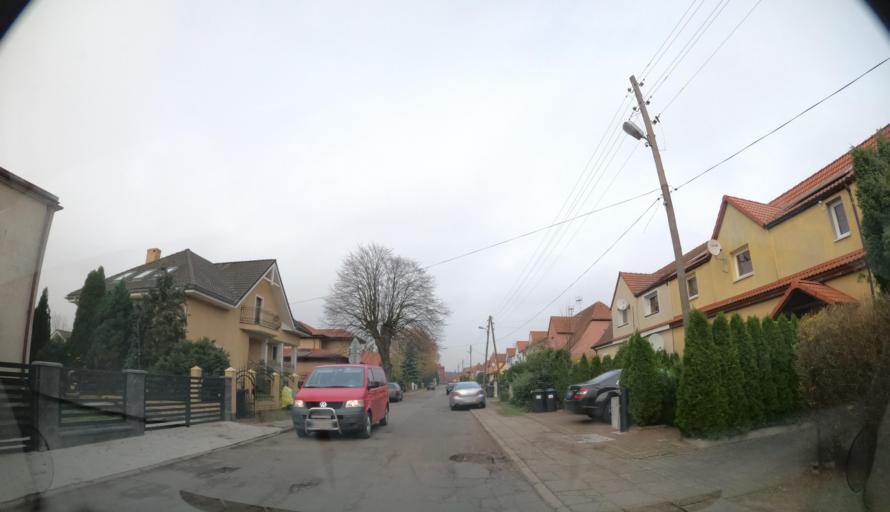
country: PL
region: West Pomeranian Voivodeship
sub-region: Powiat goleniowski
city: Goleniow
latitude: 53.5715
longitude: 14.8365
